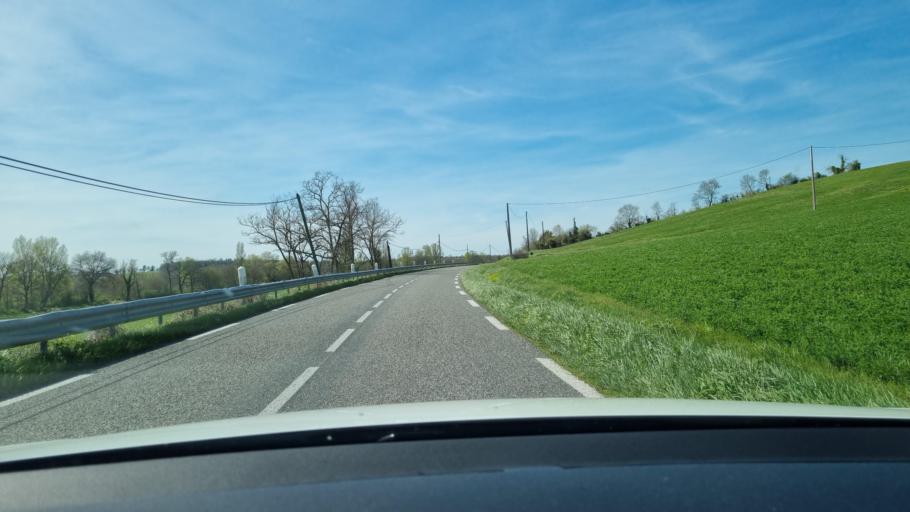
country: FR
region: Midi-Pyrenees
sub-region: Departement du Gers
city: Samatan
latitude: 43.4891
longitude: 0.9777
